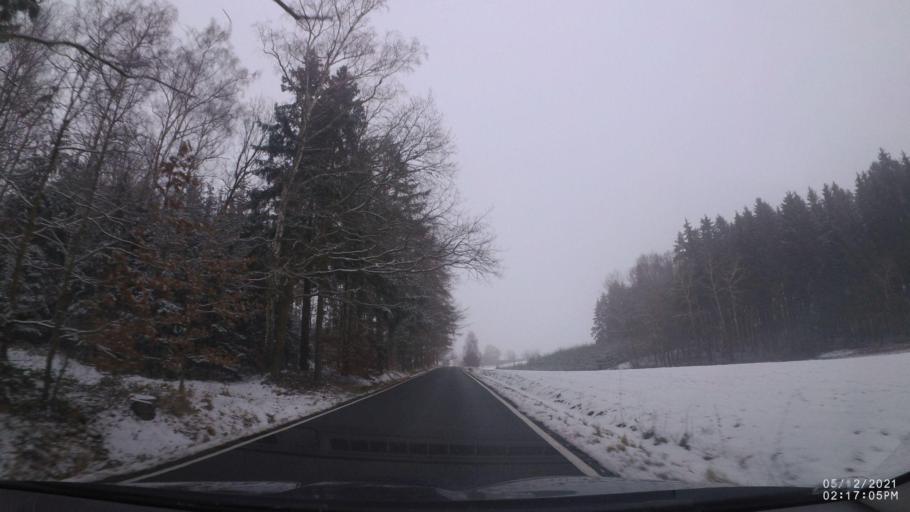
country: CZ
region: Kralovehradecky
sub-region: Okres Nachod
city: Cerveny Kostelec
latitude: 50.4669
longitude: 16.1234
